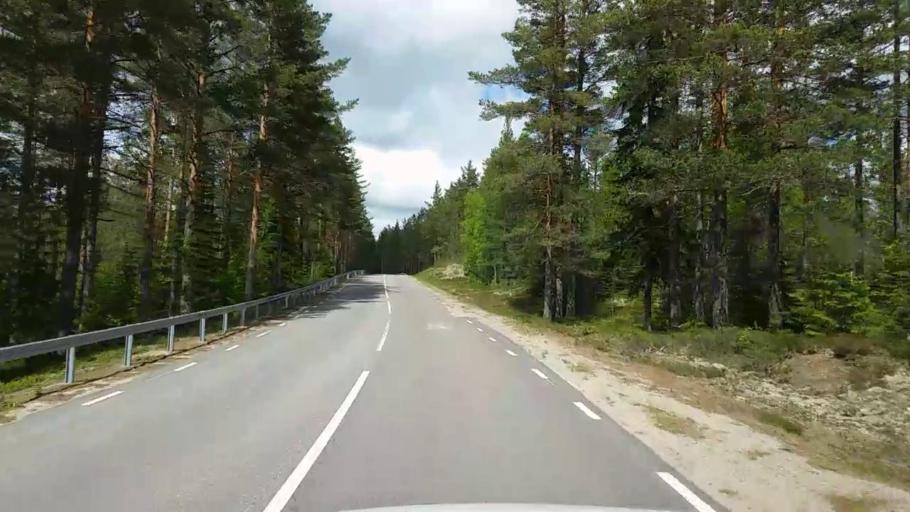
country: SE
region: Gaevleborg
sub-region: Bollnas Kommun
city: Vittsjo
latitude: 61.1322
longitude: 16.1769
